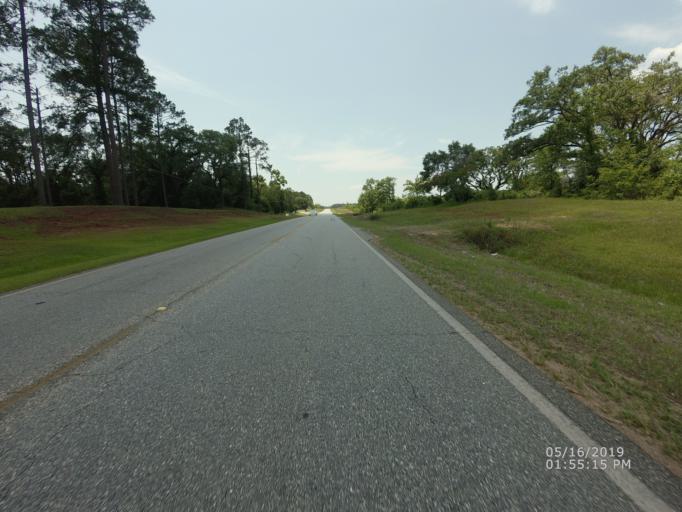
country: US
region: Georgia
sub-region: Dougherty County
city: Albany
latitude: 31.5490
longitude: -84.2463
